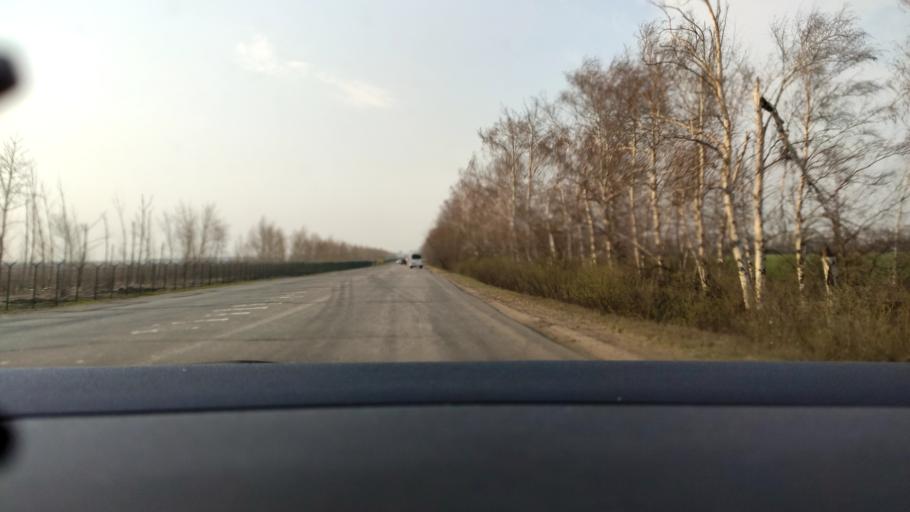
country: RU
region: Voronezj
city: Maslovka
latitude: 51.5241
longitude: 39.2966
